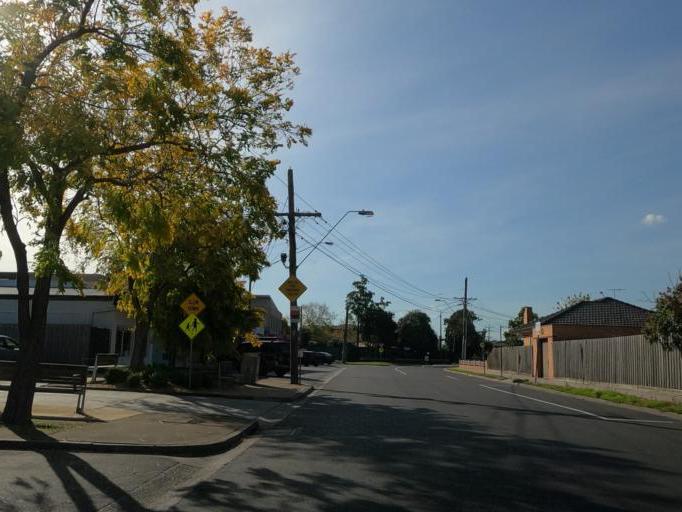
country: AU
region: Victoria
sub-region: Moonee Valley
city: Airport West
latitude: -37.7244
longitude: 144.8815
